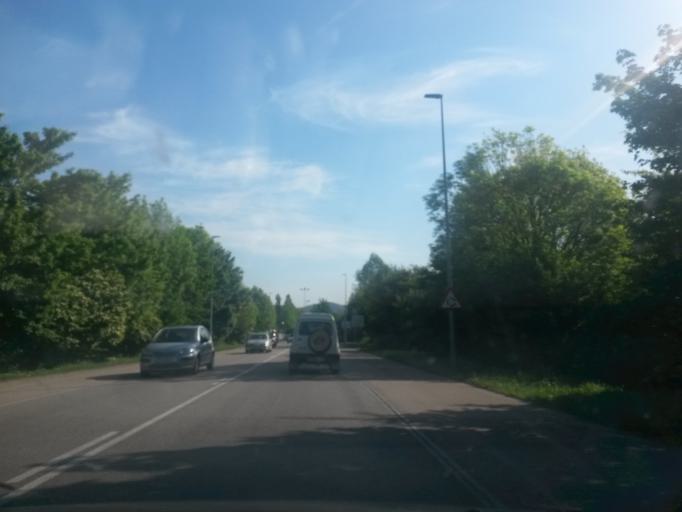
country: ES
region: Catalonia
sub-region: Provincia de Girona
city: Olot
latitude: 42.1691
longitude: 2.4836
